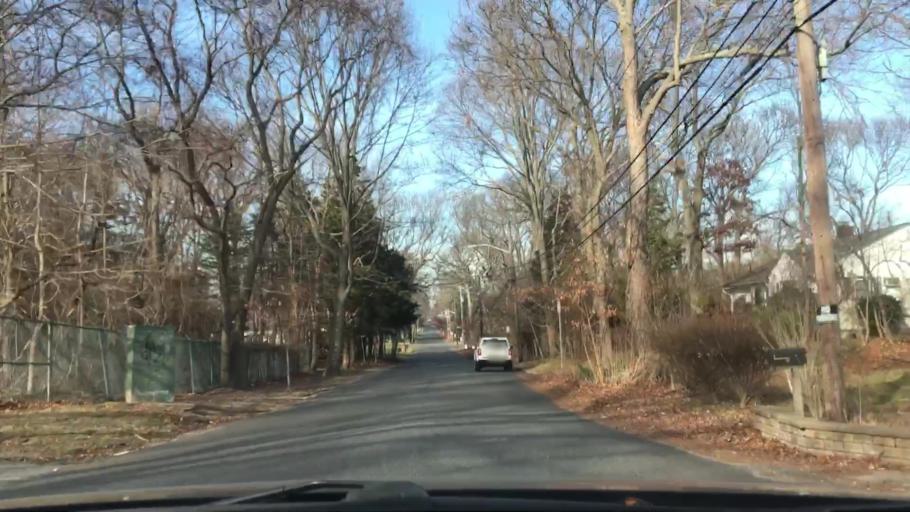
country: US
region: New York
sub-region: Suffolk County
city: Lake Grove
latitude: 40.8394
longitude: -73.1057
